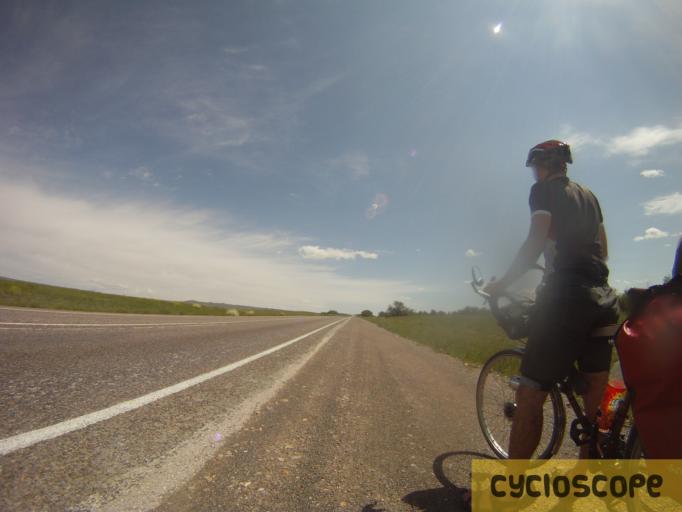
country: KZ
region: Zhambyl
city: Georgiyevka
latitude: 43.2974
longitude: 74.8838
